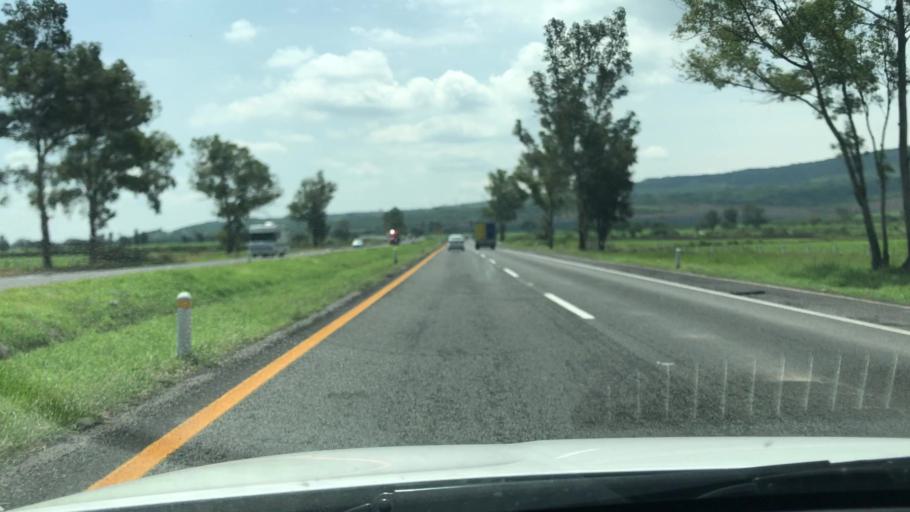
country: MX
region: Jalisco
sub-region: Zapotlan del Rey
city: Zapotlan del Rey
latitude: 20.4448
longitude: -102.8669
